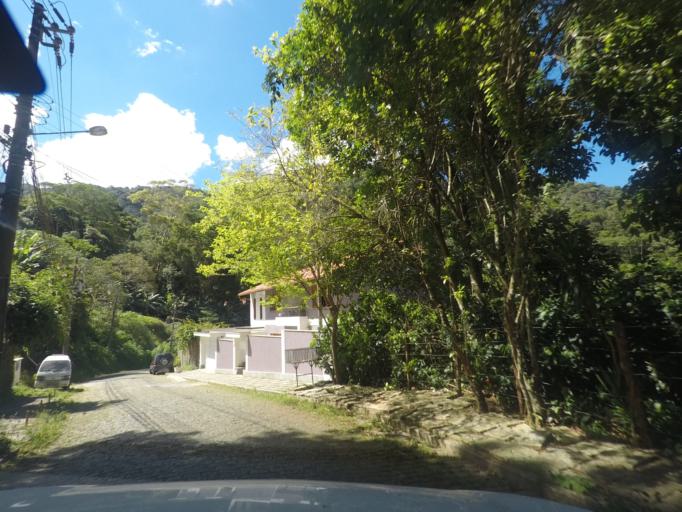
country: BR
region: Rio de Janeiro
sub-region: Teresopolis
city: Teresopolis
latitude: -22.4341
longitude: -42.9890
